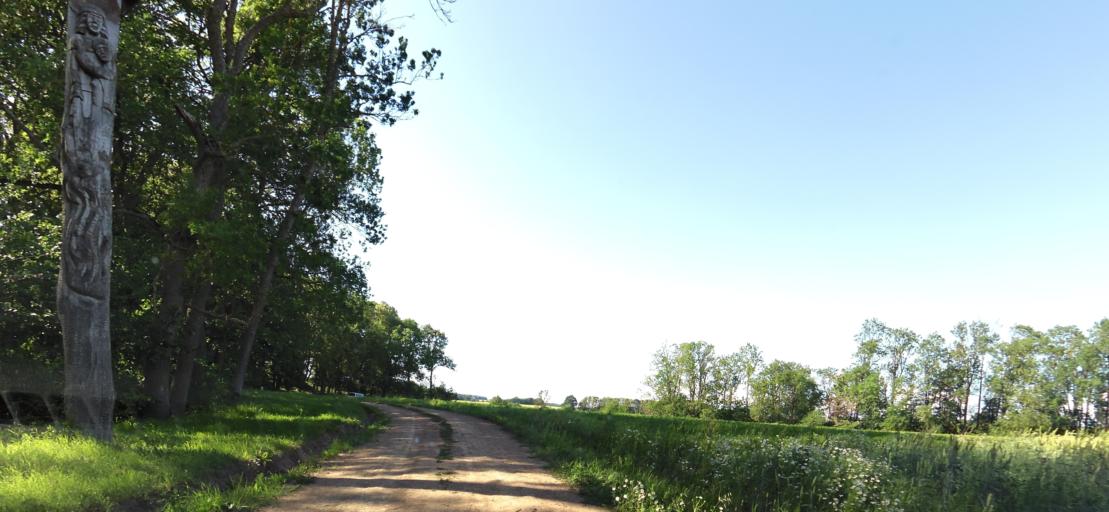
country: LT
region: Panevezys
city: Pasvalys
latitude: 56.1224
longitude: 24.4616
